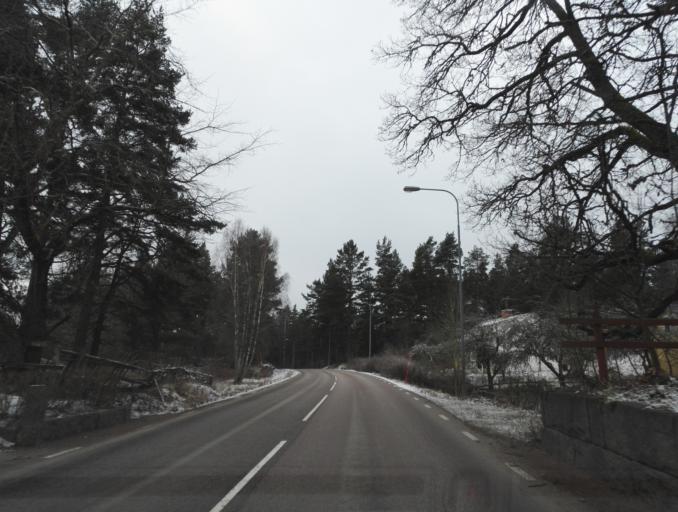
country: SE
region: Kalmar
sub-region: Hultsfreds Kommun
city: Virserum
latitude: 57.4002
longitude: 15.6038
